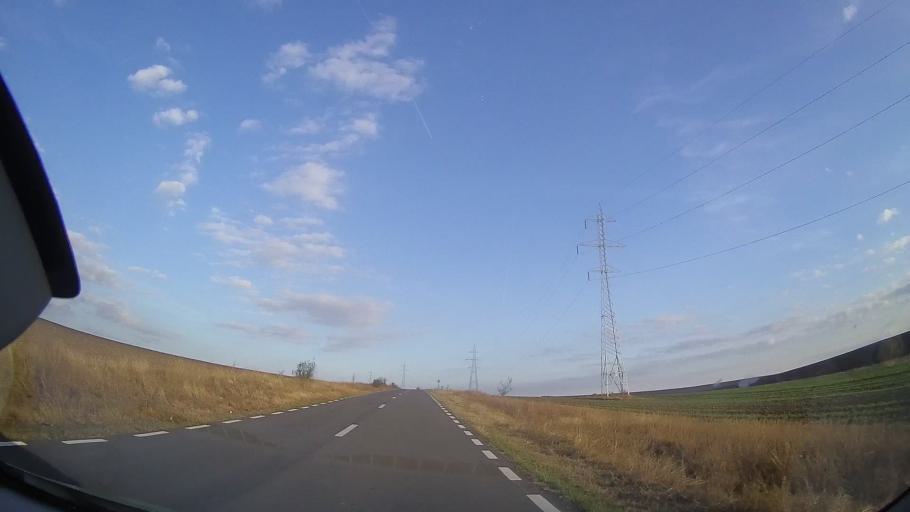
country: RO
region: Constanta
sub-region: Comuna Chirnogeni
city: Plopeni
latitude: 43.9530
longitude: 28.1552
